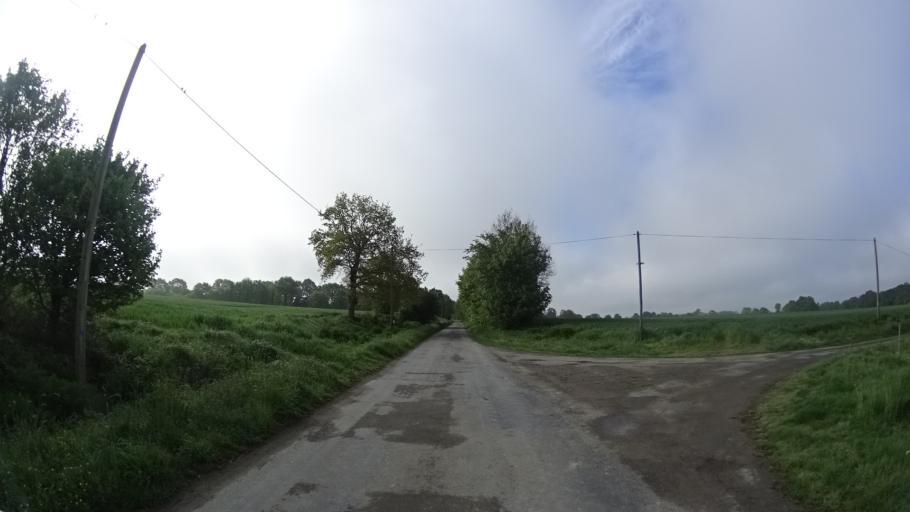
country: FR
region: Brittany
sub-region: Departement d'Ille-et-Vilaine
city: Mordelles
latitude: 48.0901
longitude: -1.8563
